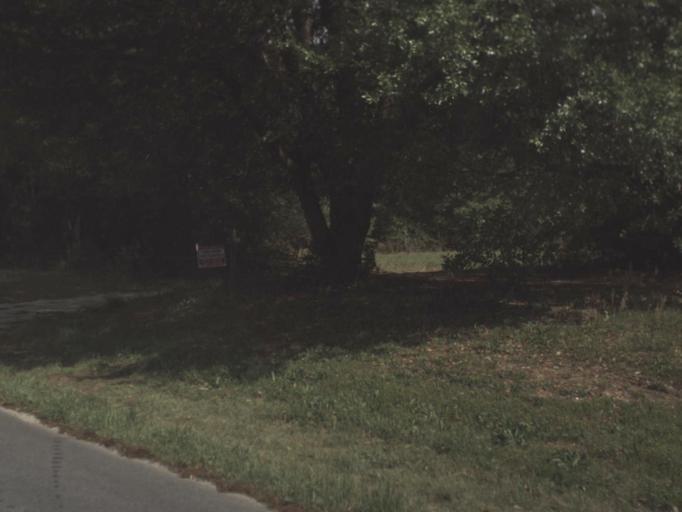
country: US
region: Florida
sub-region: Santa Rosa County
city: East Milton
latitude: 30.6383
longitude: -86.9574
